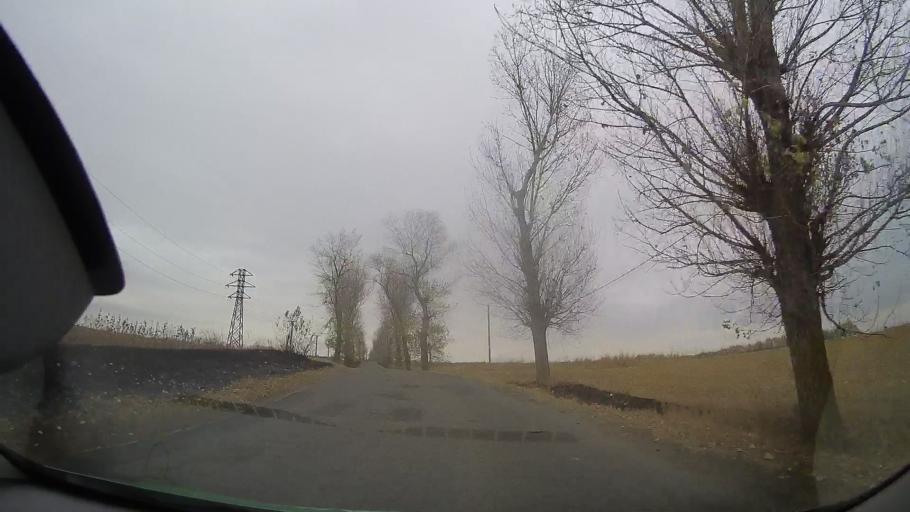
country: RO
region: Buzau
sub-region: Comuna Rusetu
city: Rusetu
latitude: 44.9485
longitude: 27.2296
